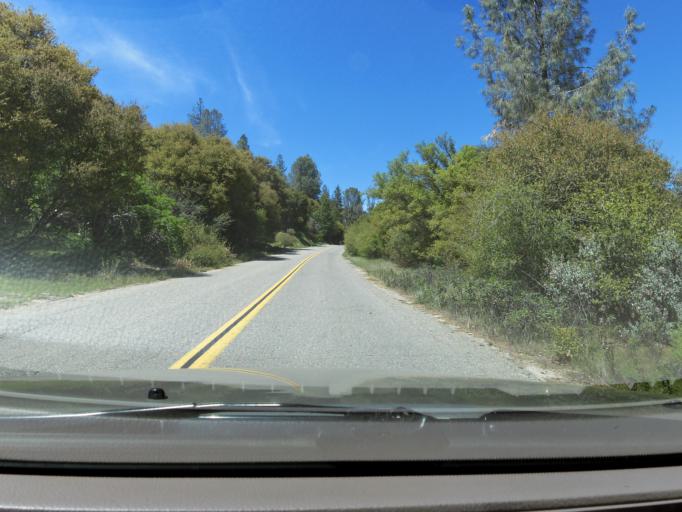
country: US
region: California
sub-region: Fresno County
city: Auberry
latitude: 37.2353
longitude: -119.5160
